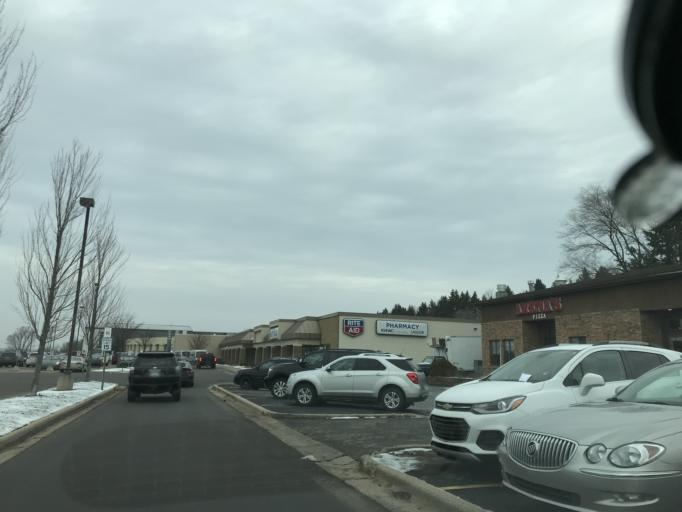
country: US
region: Michigan
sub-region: Kent County
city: Rockford
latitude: 43.1176
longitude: -85.5467
